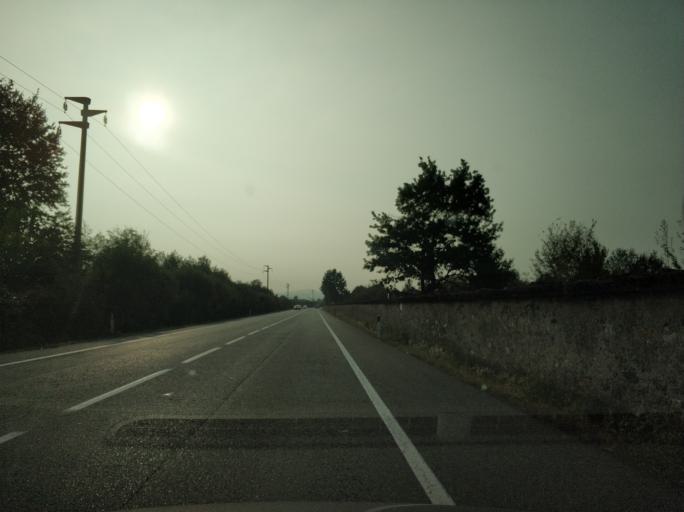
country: IT
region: Piedmont
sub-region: Provincia di Torino
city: Caselle Torinese
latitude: 45.1602
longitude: 7.6054
